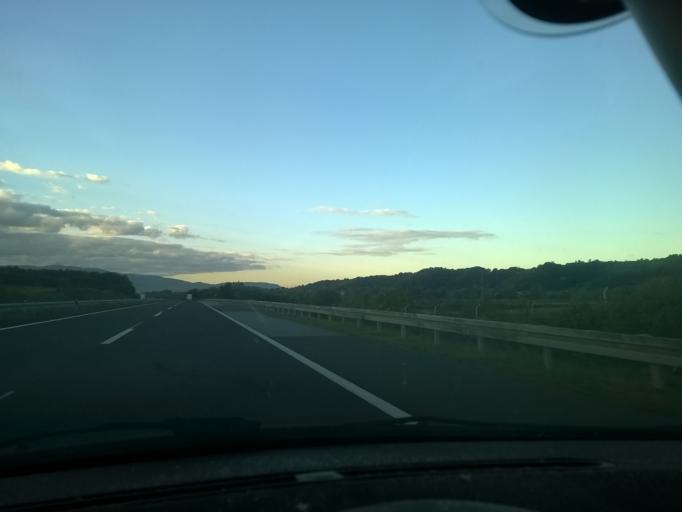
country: HR
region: Krapinsko-Zagorska
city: Zabok
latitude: 46.0598
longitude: 15.9192
